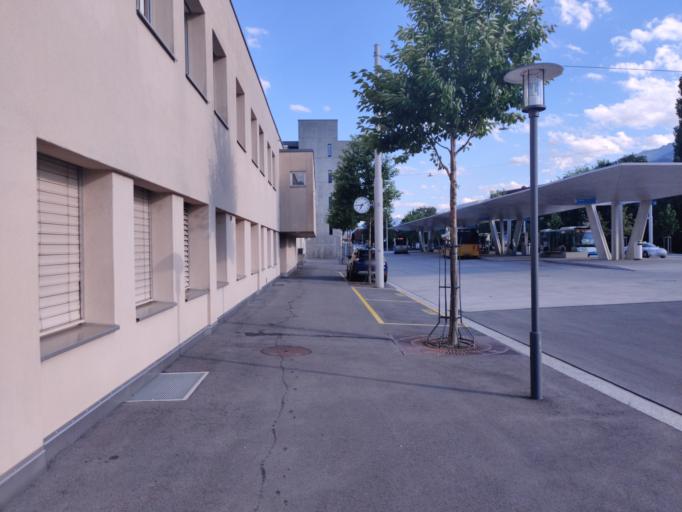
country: CH
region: Saint Gallen
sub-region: Wahlkreis Werdenberg
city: Buchs
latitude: 47.1690
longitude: 9.4782
